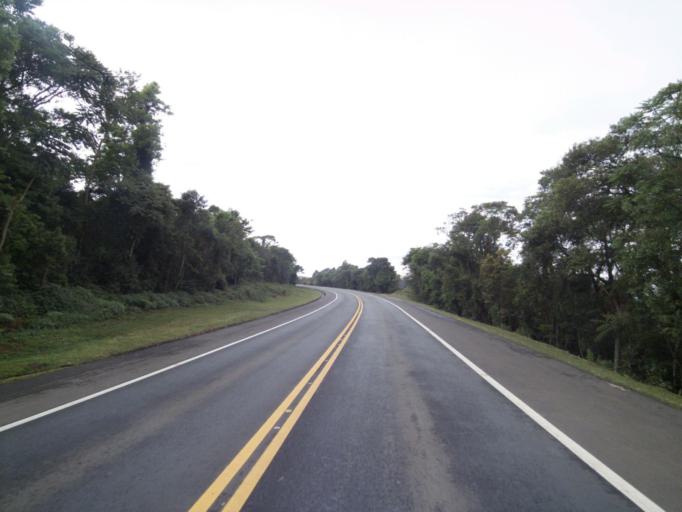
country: BR
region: Parana
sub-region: Irati
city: Irati
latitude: -25.4525
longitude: -50.6450
